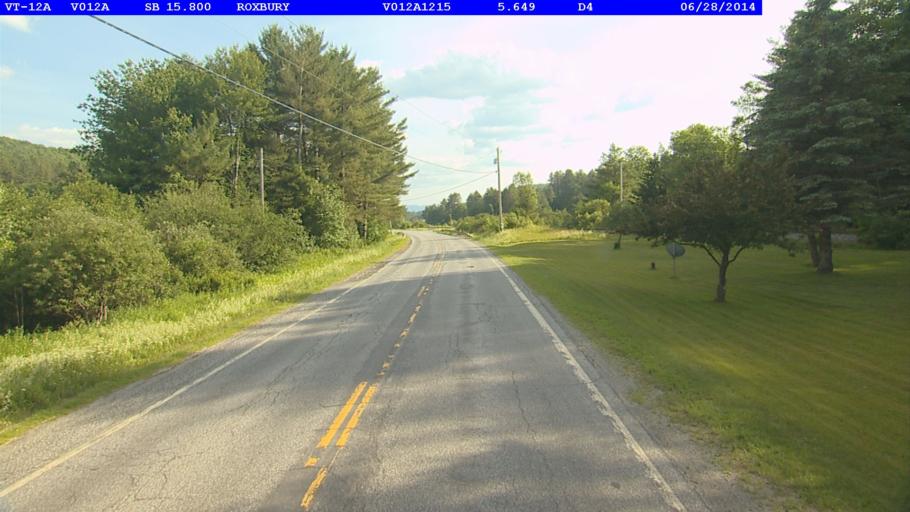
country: US
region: Vermont
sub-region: Washington County
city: Northfield
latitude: 44.1064
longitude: -72.7288
